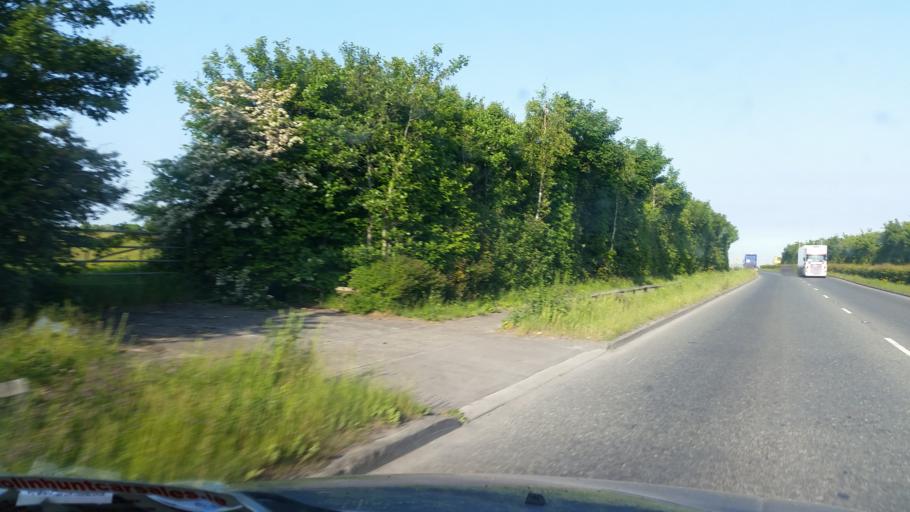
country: IE
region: Leinster
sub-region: Dublin City
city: Finglas
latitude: 53.4247
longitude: -6.3093
